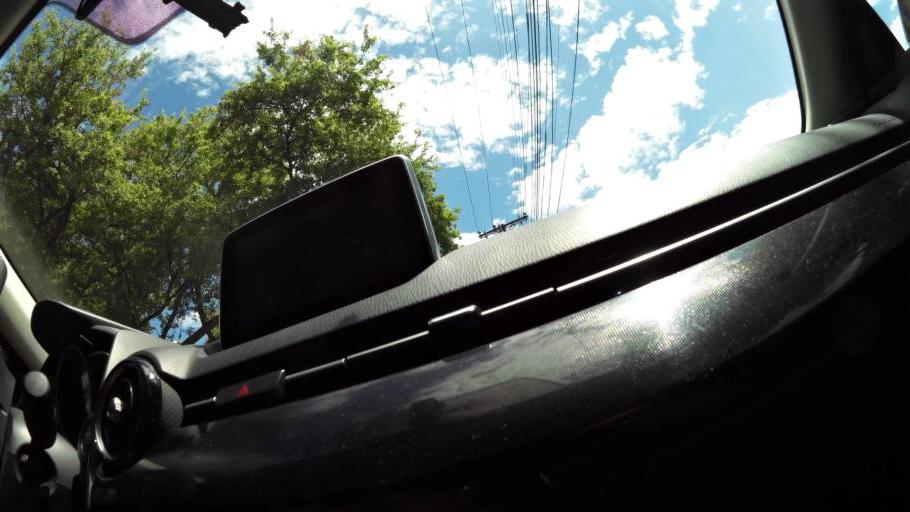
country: CO
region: Valle del Cauca
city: Cali
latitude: 3.3831
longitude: -76.5203
